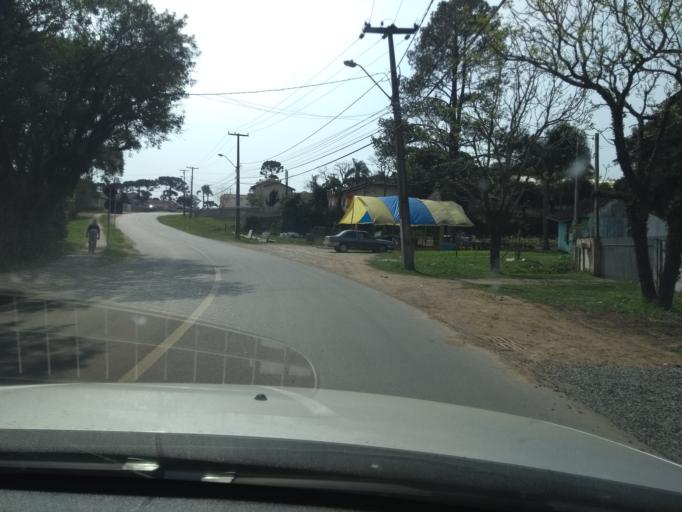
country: BR
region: Parana
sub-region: Araucaria
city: Araucaria
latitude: -25.6184
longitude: -49.3463
